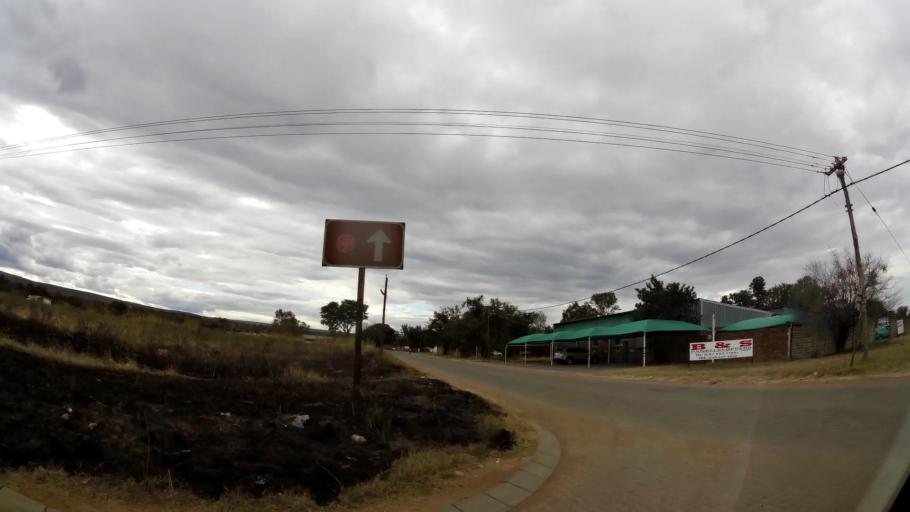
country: ZA
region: Limpopo
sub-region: Waterberg District Municipality
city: Modimolle
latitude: -24.7086
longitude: 28.4192
